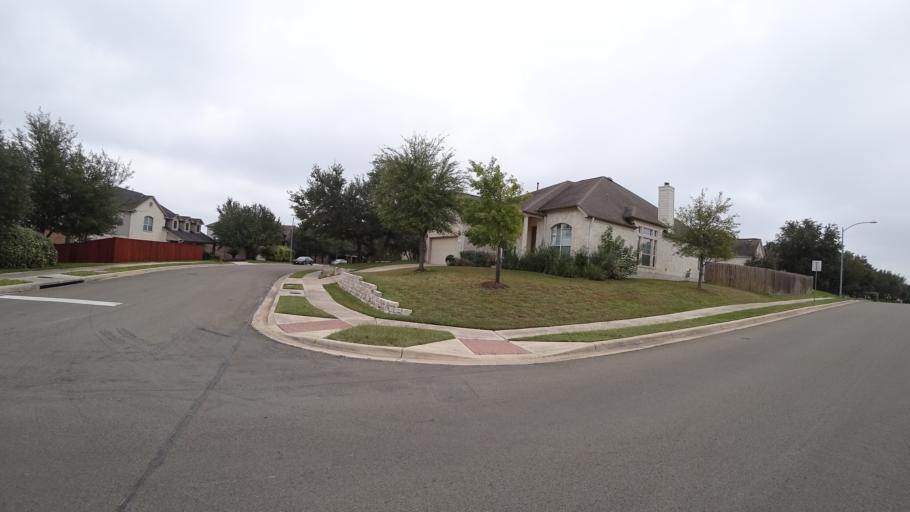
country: US
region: Texas
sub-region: Travis County
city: Barton Creek
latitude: 30.2427
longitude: -97.8994
